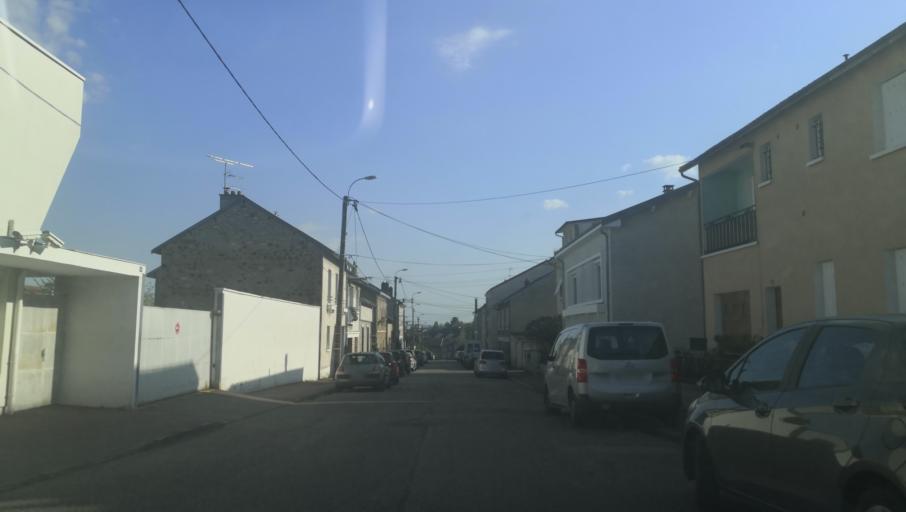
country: FR
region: Limousin
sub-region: Departement de la Haute-Vienne
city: Limoges
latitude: 45.8473
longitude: 1.2486
